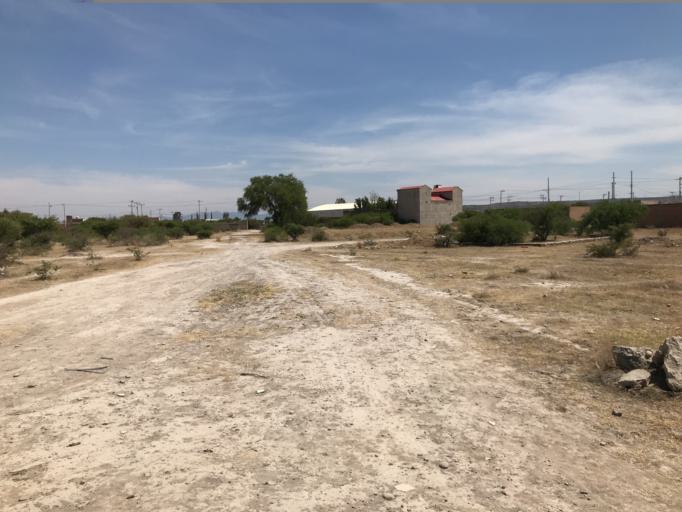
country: MX
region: Durango
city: Victoria de Durango
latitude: 23.9804
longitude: -104.6833
